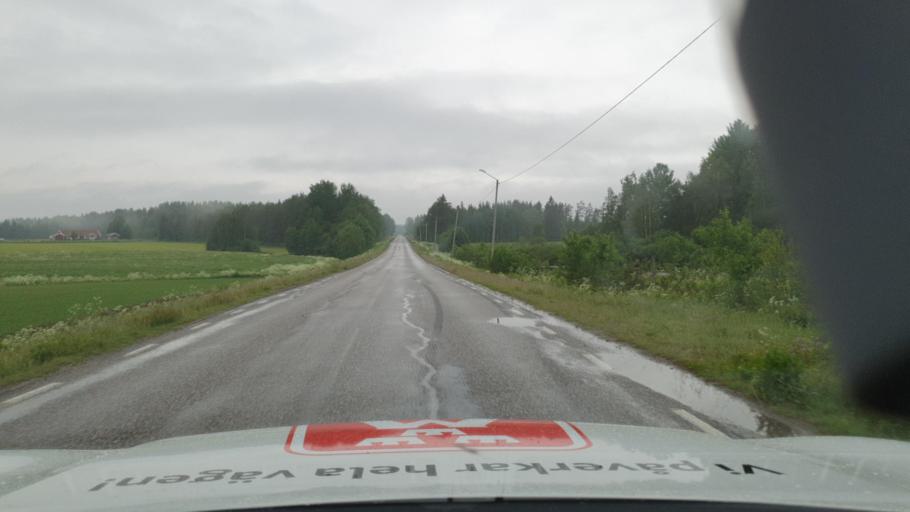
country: SE
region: Vaesterbotten
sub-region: Nordmalings Kommun
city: Nordmaling
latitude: 63.7917
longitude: 19.5471
